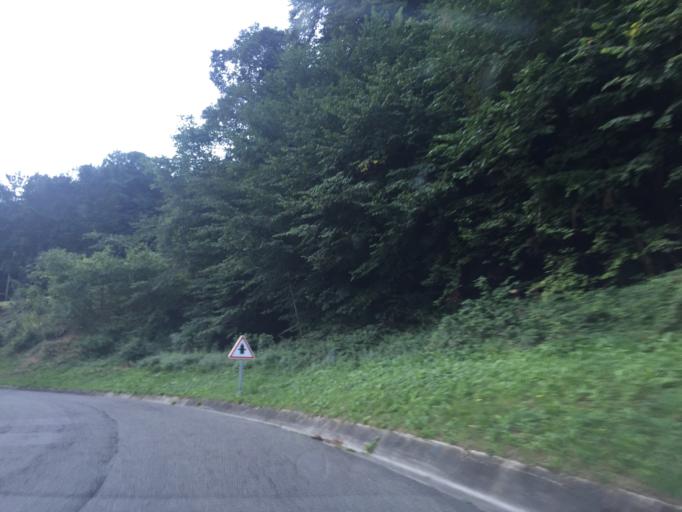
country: FR
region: Midi-Pyrenees
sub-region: Departement des Hautes-Pyrenees
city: Cauterets
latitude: 42.8864
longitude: -0.1157
